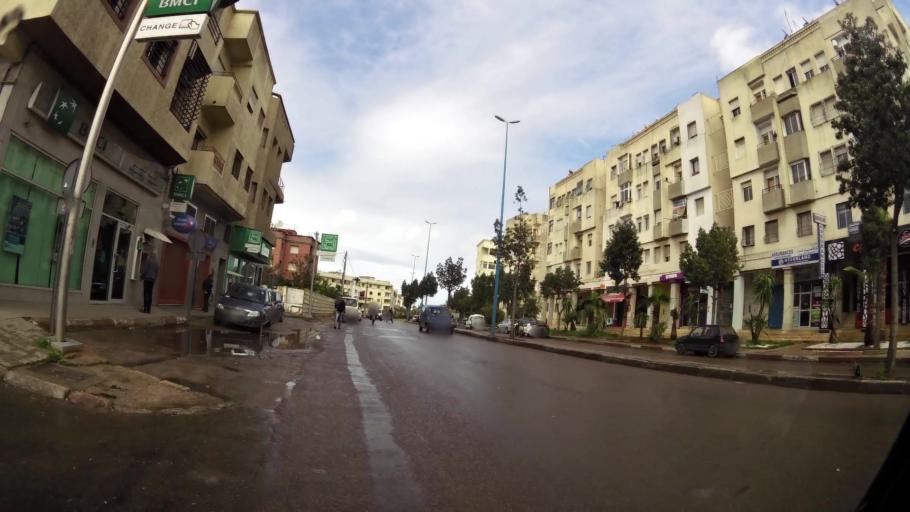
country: MA
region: Grand Casablanca
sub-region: Casablanca
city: Casablanca
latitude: 33.5306
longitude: -7.6485
